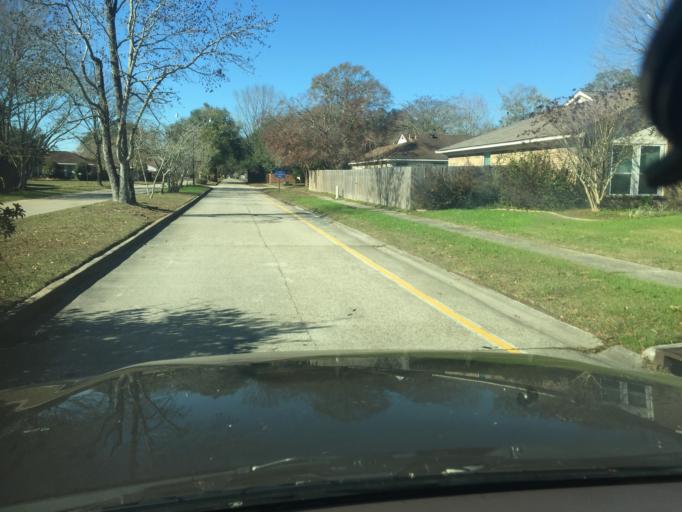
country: US
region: Louisiana
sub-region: Saint Tammany Parish
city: Slidell
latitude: 30.3009
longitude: -89.7263
